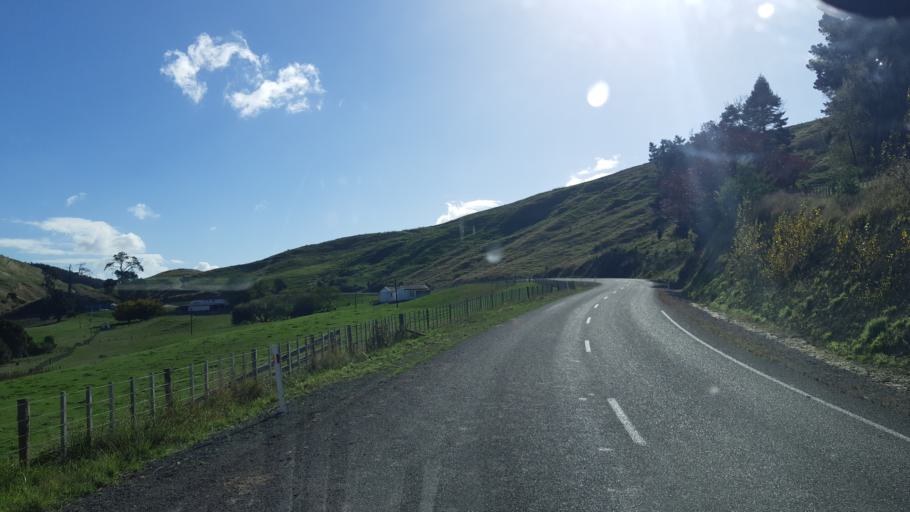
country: NZ
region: Manawatu-Wanganui
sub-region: Rangitikei District
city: Bulls
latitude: -39.9036
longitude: 175.3495
